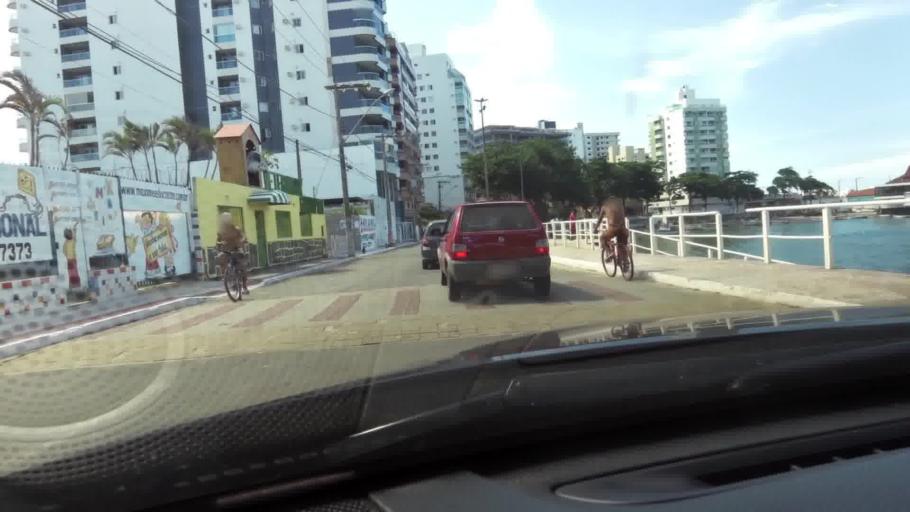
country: BR
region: Espirito Santo
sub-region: Guarapari
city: Guarapari
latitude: -20.6634
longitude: -40.4976
